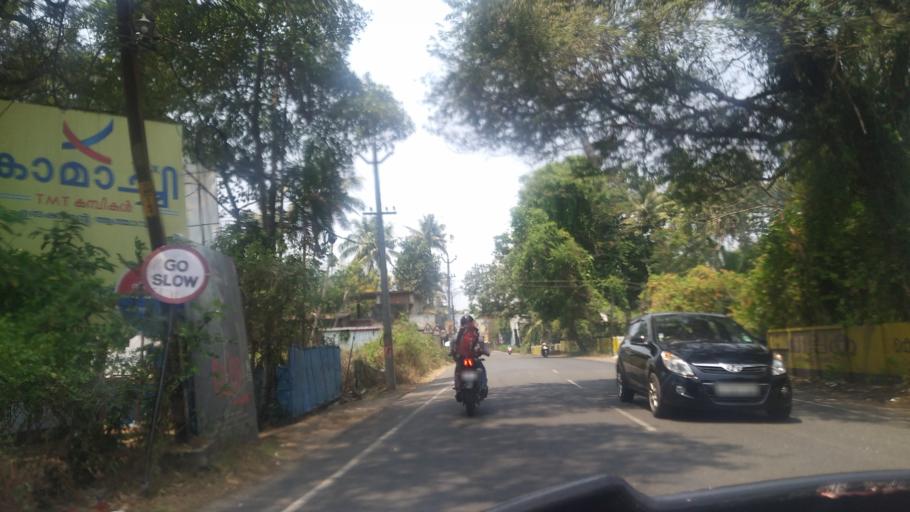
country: IN
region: Kerala
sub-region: Thrissur District
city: Kodungallur
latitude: 10.2469
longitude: 76.1891
